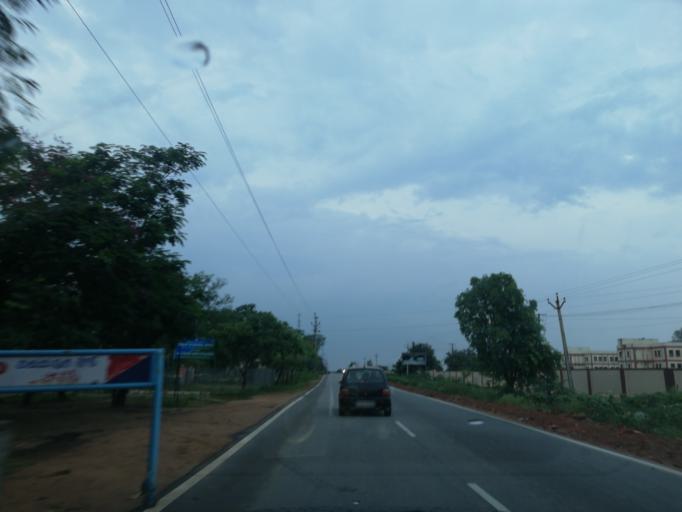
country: IN
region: Andhra Pradesh
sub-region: Guntur
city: Macherla
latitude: 16.6174
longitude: 79.2957
